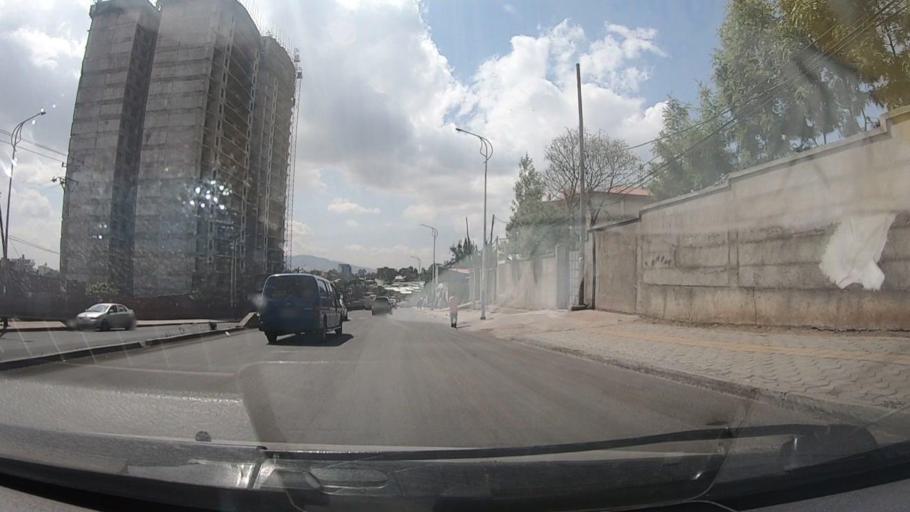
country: ET
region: Adis Abeba
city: Addis Ababa
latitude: 8.9859
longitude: 38.7208
